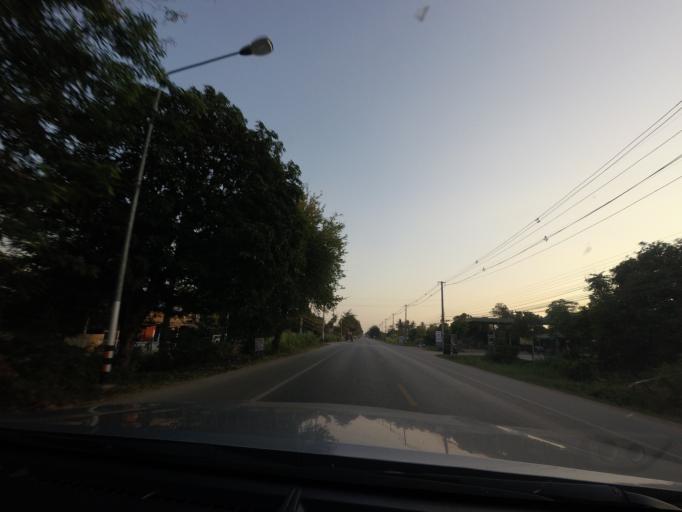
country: TH
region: Sukhothai
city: Si Samrong
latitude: 17.1355
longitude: 99.8501
